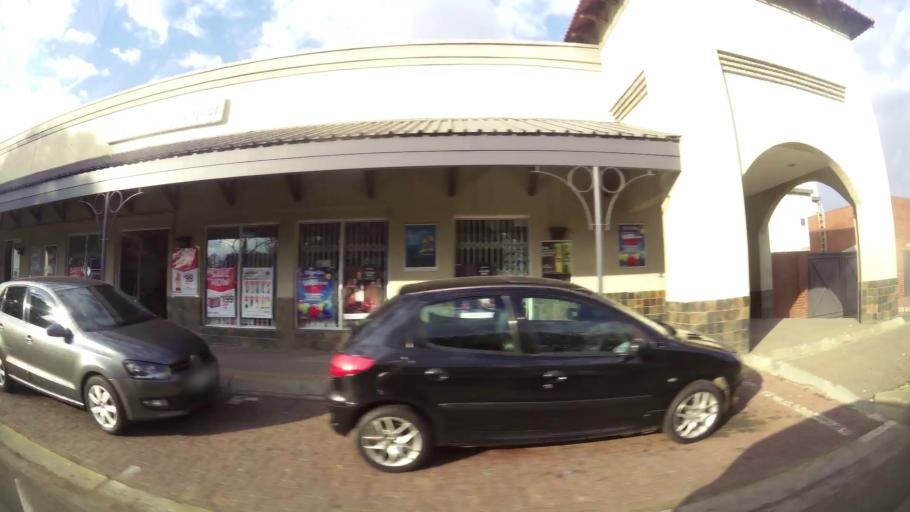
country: ZA
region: Orange Free State
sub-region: Fezile Dabi District Municipality
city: Sasolburg
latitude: -26.8163
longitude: 27.8265
